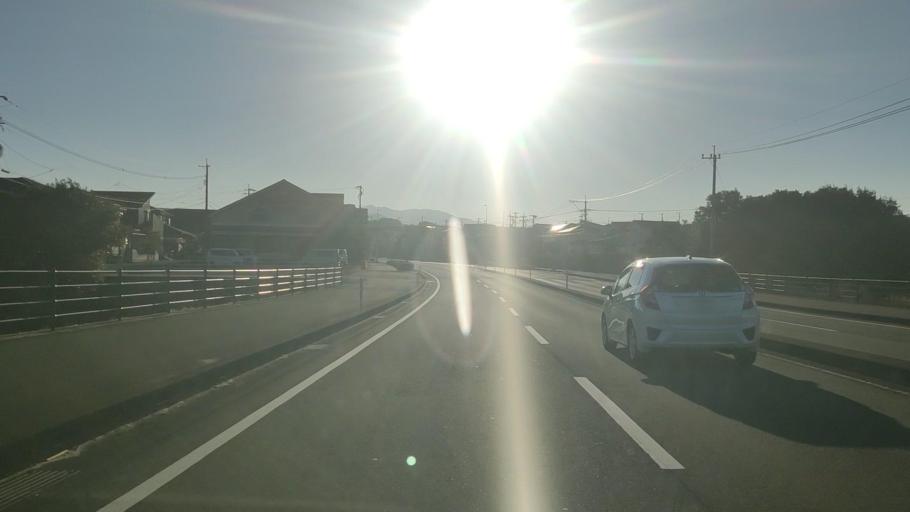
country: JP
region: Miyazaki
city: Miyazaki-shi
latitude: 31.8817
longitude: 131.3951
